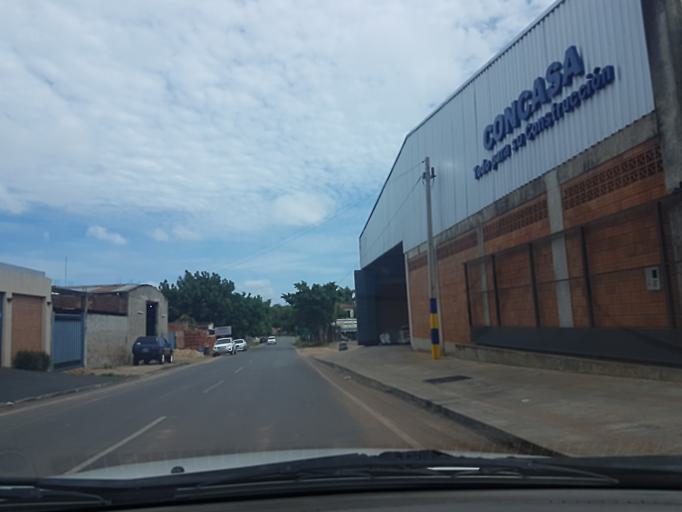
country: PY
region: Central
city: San Lorenzo
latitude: -25.2630
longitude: -57.4814
